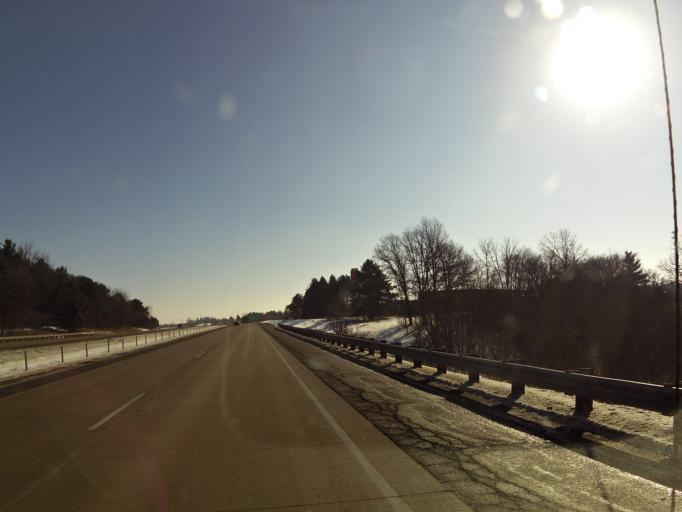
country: US
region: Wisconsin
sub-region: Dunn County
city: Menomonie
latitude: 44.9073
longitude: -91.9427
